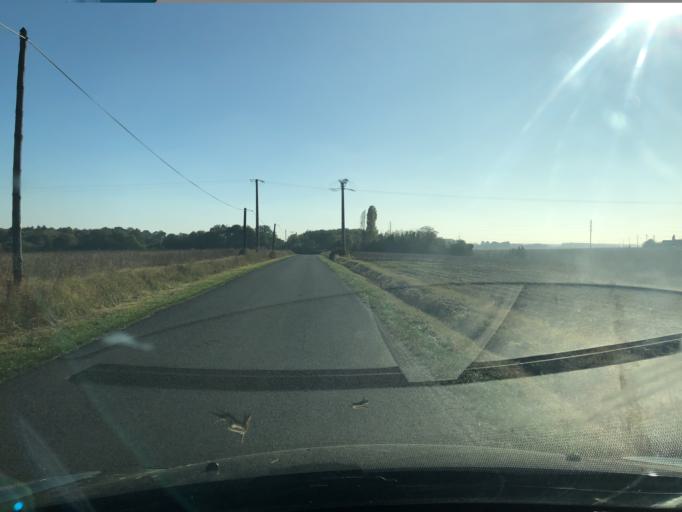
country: FR
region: Centre
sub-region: Departement d'Indre-et-Loire
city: Neuvy-le-Roi
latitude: 47.6291
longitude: 0.6001
